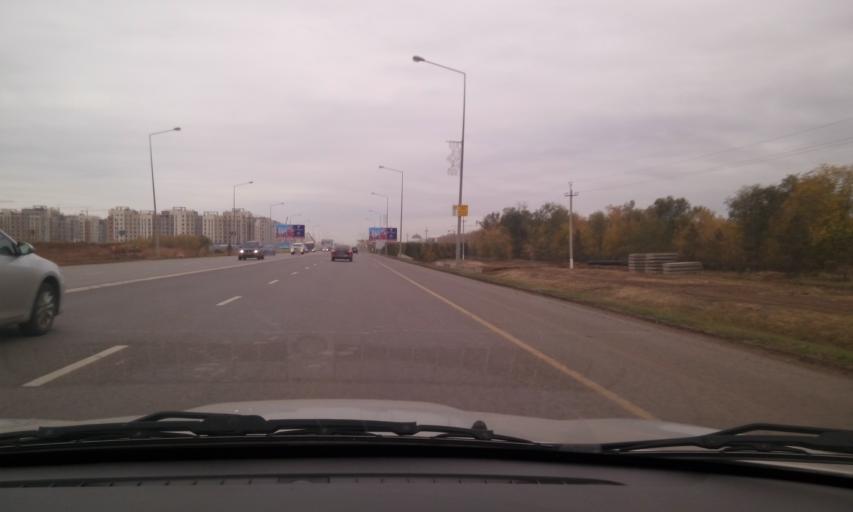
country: KZ
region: Astana Qalasy
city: Astana
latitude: 51.1032
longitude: 71.4075
